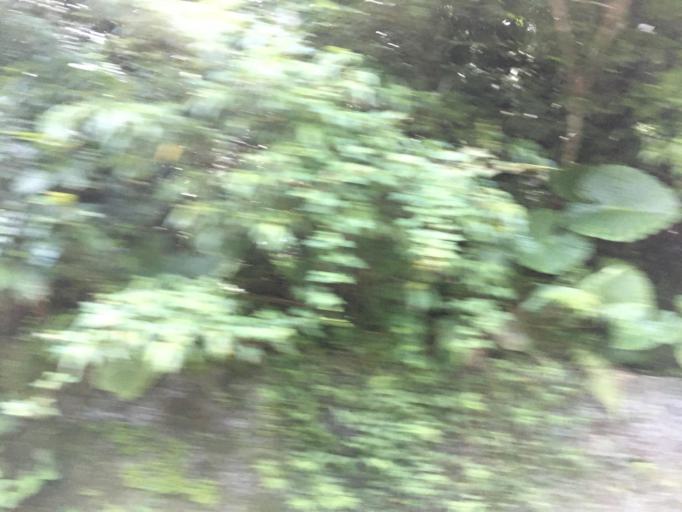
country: TW
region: Taiwan
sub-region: Yilan
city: Yilan
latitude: 24.8157
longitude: 121.7328
